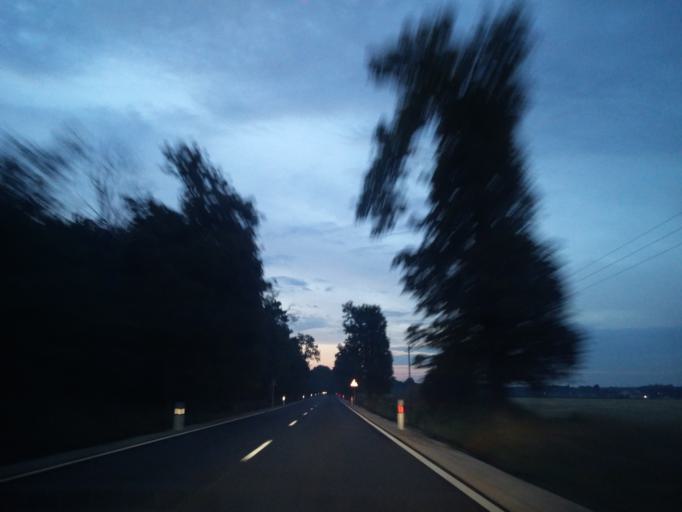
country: HU
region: Fejer
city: Lovasbereny
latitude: 47.3022
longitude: 18.5379
